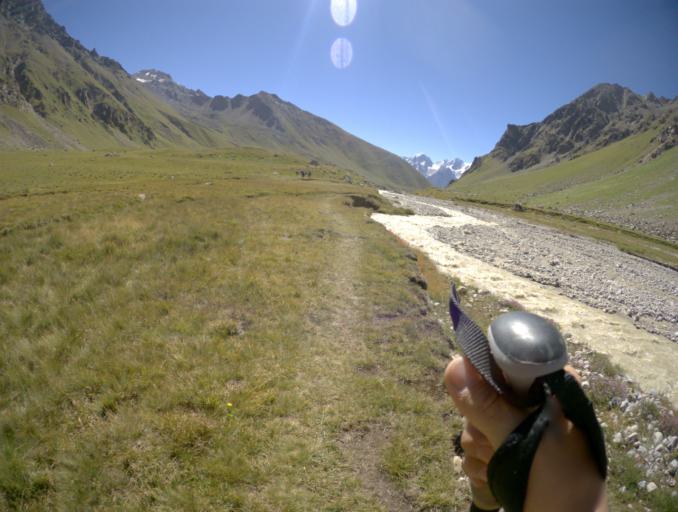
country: RU
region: Kabardino-Balkariya
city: Terskol
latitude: 43.3184
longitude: 42.5781
